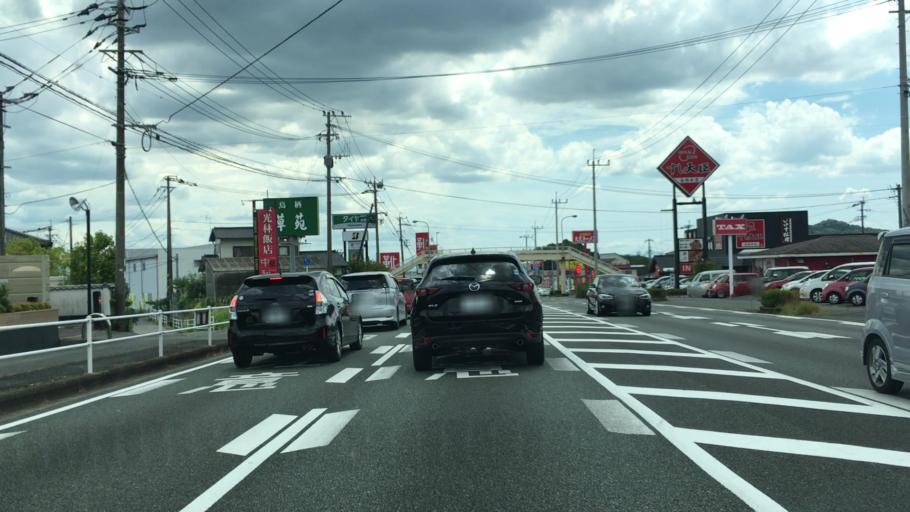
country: JP
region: Saga Prefecture
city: Tosu
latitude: 33.3862
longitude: 130.4997
